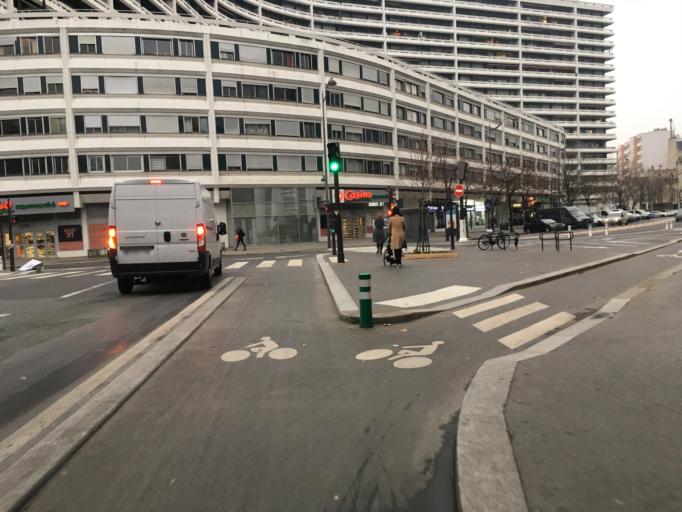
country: FR
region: Ile-de-France
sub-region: Departement des Hauts-de-Seine
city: Vanves
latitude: 48.8358
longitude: 2.2814
